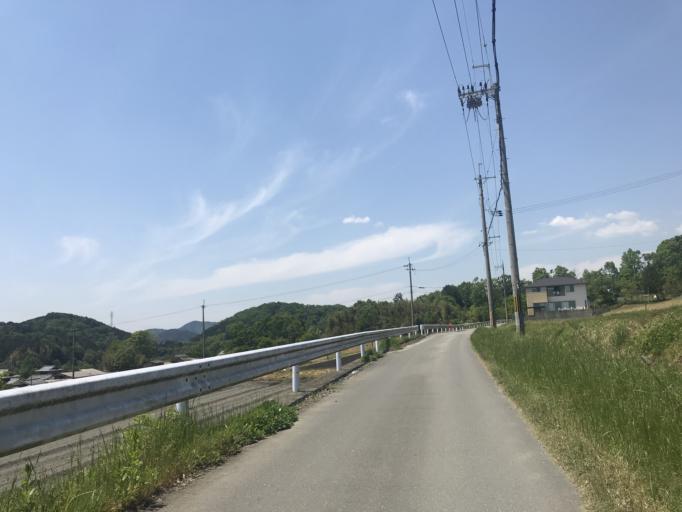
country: JP
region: Kyoto
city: Kameoka
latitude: 35.0652
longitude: 135.5721
